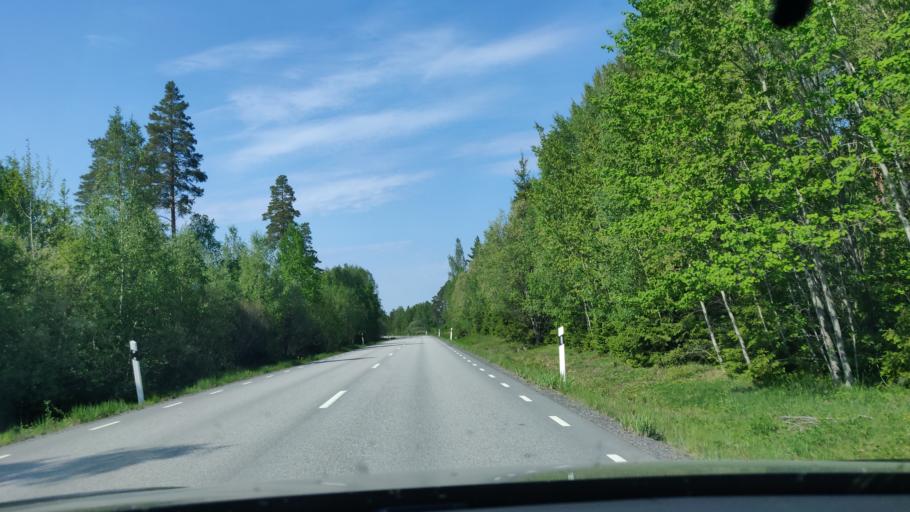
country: SE
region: Uppsala
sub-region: Heby Kommun
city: OEstervala
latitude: 60.1370
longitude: 17.2173
